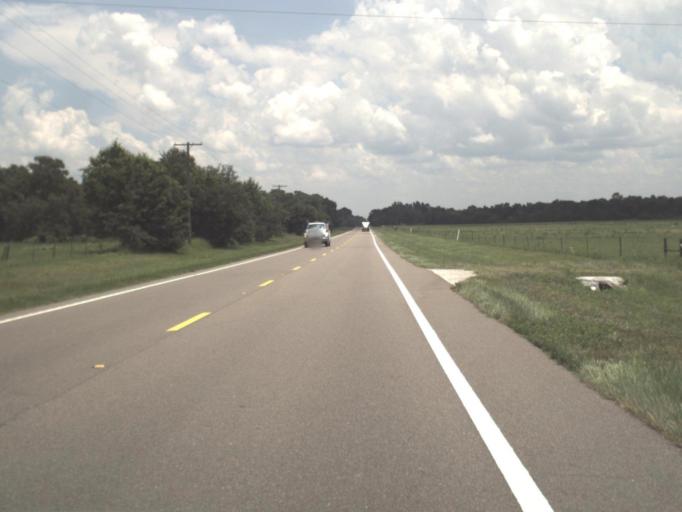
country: US
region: Florida
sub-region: Hillsborough County
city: Balm
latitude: 27.7048
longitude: -82.2162
